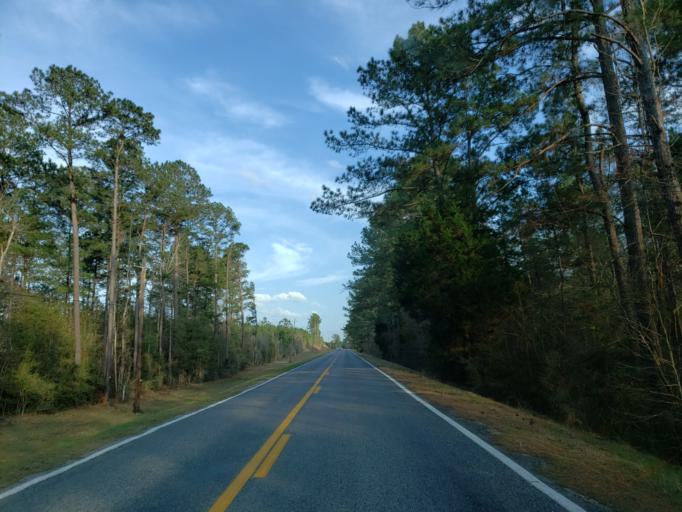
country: US
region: Mississippi
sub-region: Clarke County
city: Stonewall
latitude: 32.1770
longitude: -88.7967
